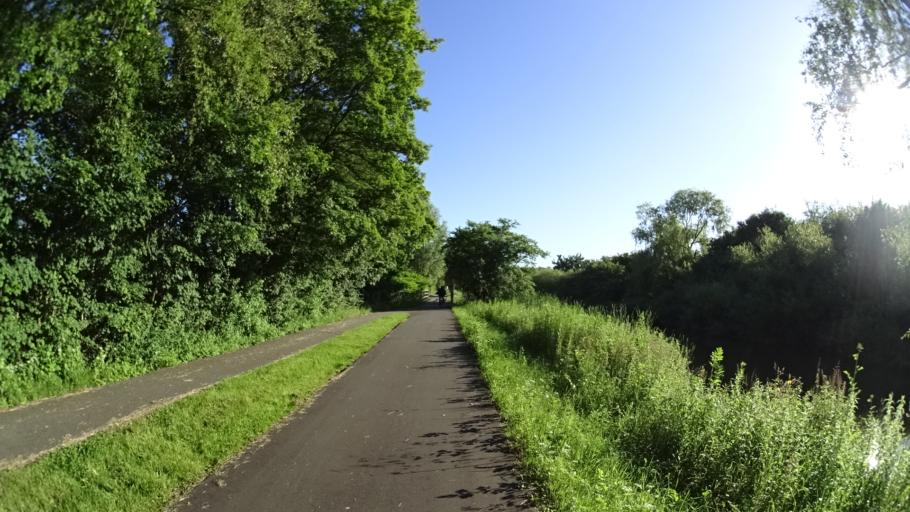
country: DK
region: Central Jutland
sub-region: Arhus Kommune
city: Arhus
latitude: 56.1502
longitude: 10.1774
